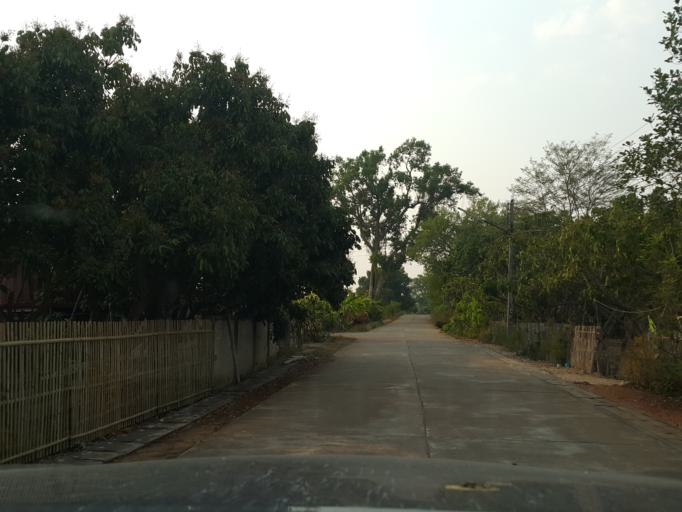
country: TH
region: Lamphun
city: Li
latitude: 17.8065
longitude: 98.9502
